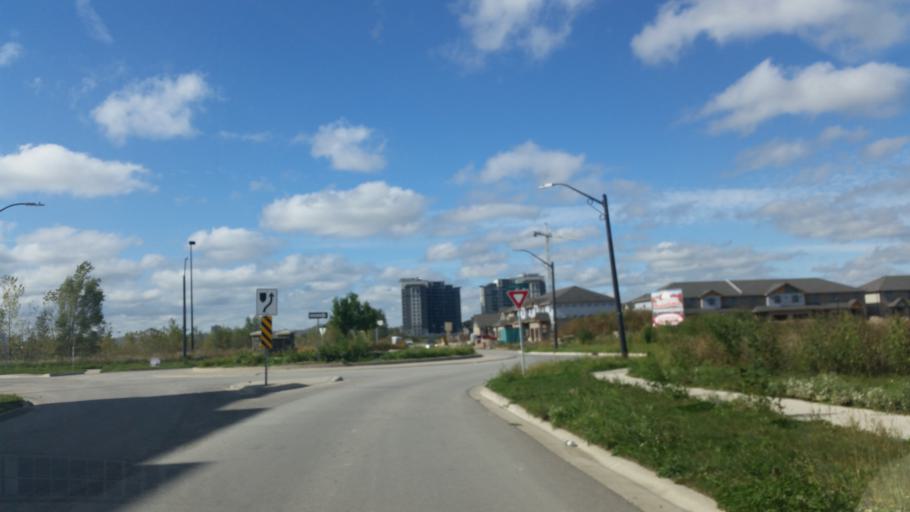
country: CA
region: Ontario
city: London
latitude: 43.0154
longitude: -81.3319
